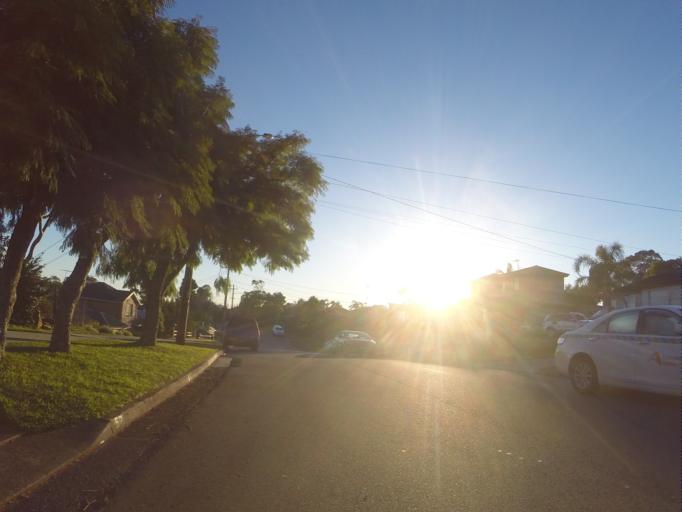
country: AU
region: New South Wales
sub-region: Sutherland Shire
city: Engadine
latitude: -34.0502
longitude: 151.0115
